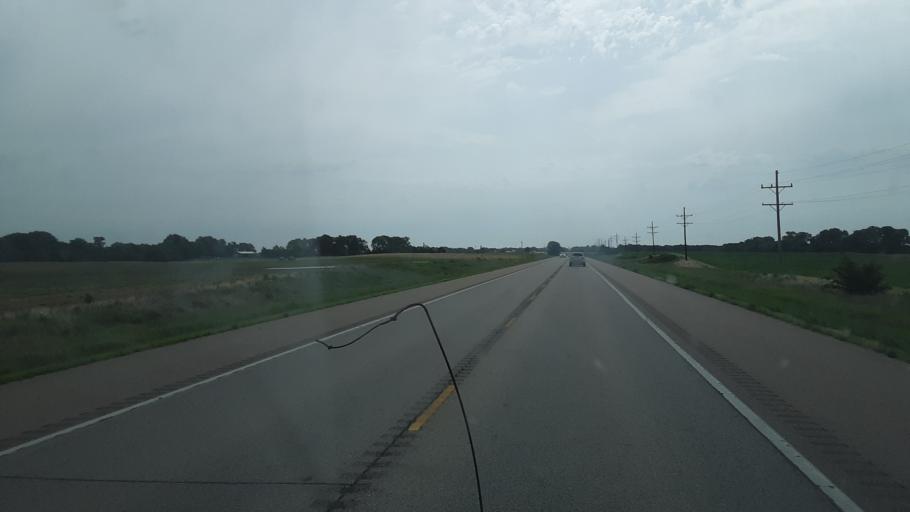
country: US
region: Kansas
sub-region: Stafford County
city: Stafford
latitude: 37.9551
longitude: -98.4444
